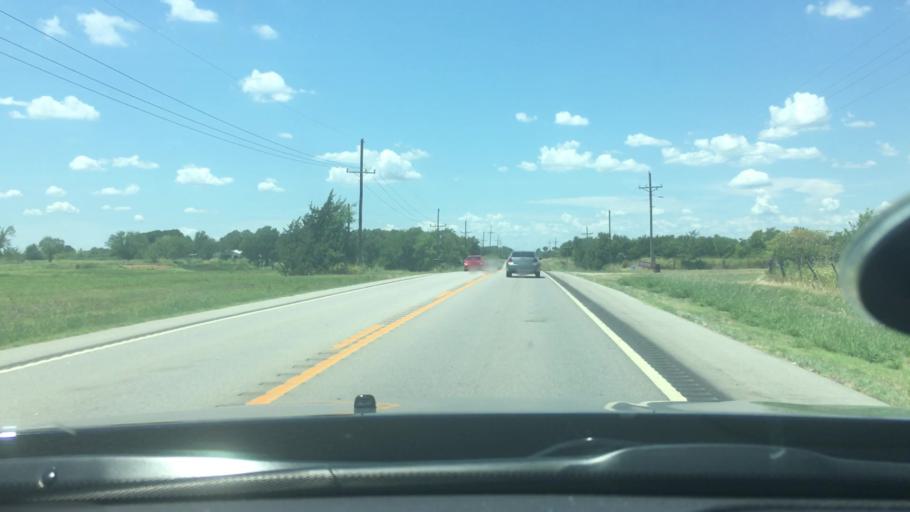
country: US
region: Oklahoma
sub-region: Bryan County
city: Durant
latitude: 33.9975
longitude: -96.2727
